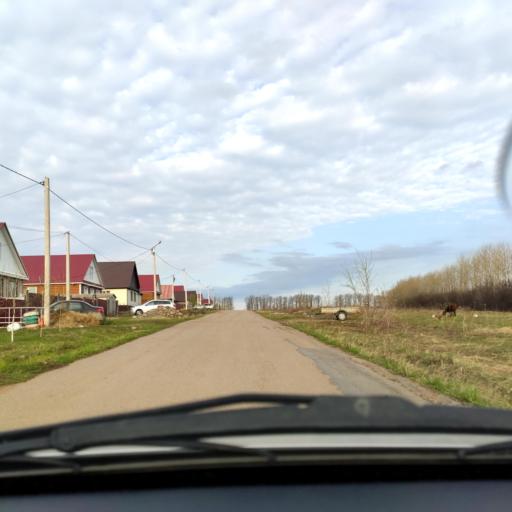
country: RU
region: Bashkortostan
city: Iglino
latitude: 54.7927
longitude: 56.2756
